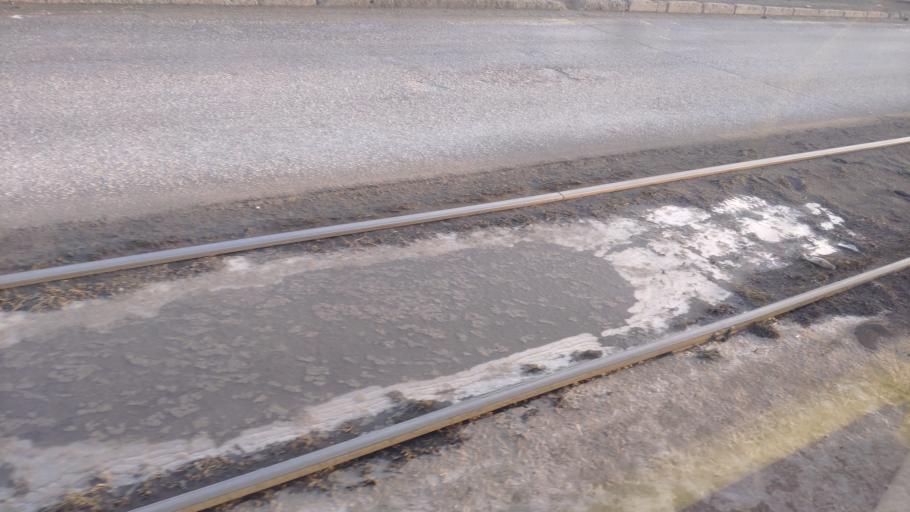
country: RU
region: Chelyabinsk
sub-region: Gorod Magnitogorsk
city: Magnitogorsk
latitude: 53.4222
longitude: 59.0159
